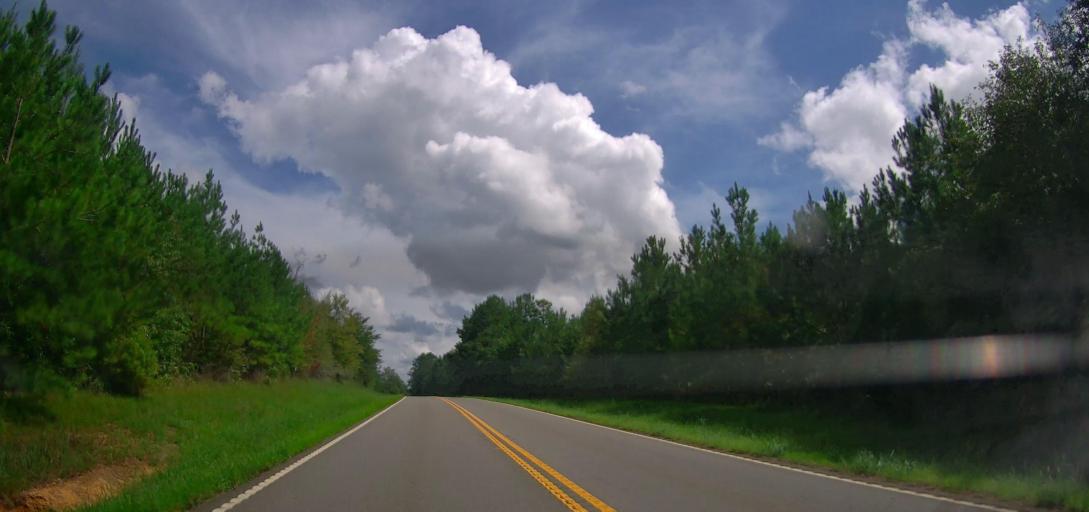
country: US
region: Georgia
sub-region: Talbot County
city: Talbotton
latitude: 32.6653
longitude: -84.5172
